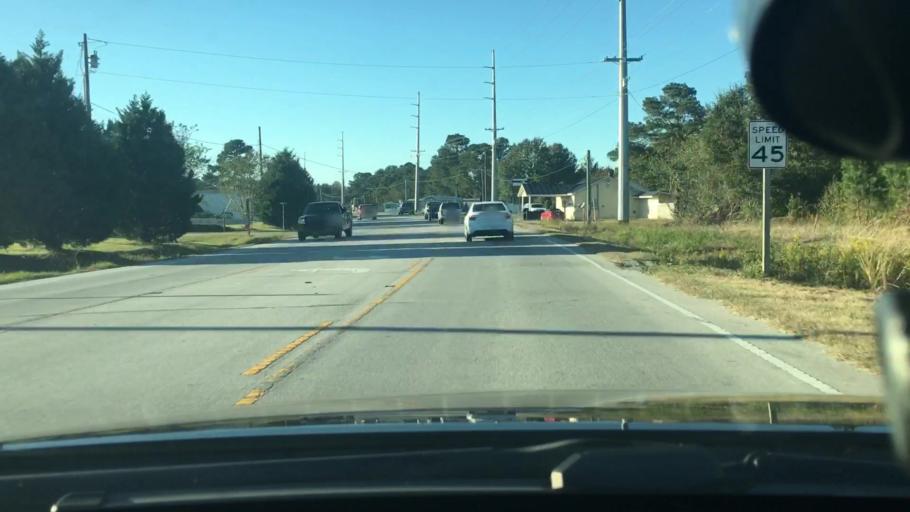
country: US
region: North Carolina
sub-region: Pitt County
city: Windsor
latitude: 35.5545
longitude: -77.3294
